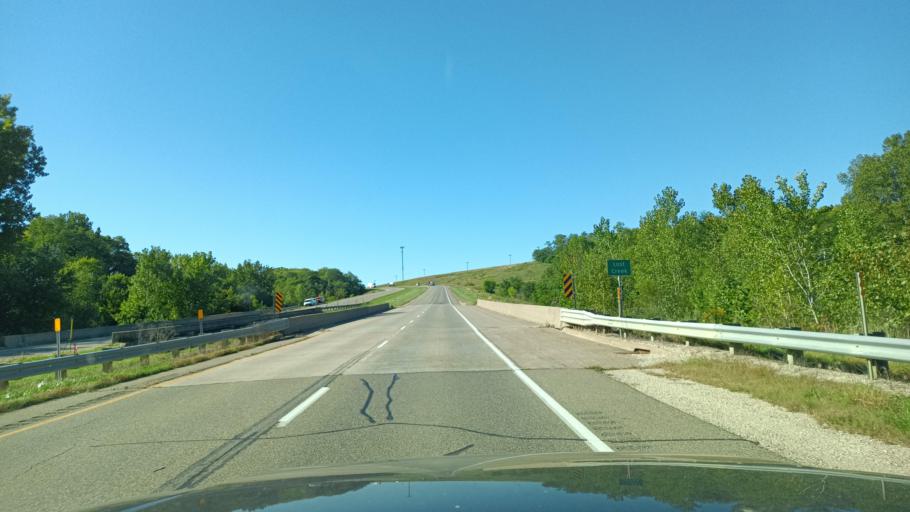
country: US
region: Iowa
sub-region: Lee County
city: Fort Madison
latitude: 40.6947
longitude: -91.2464
